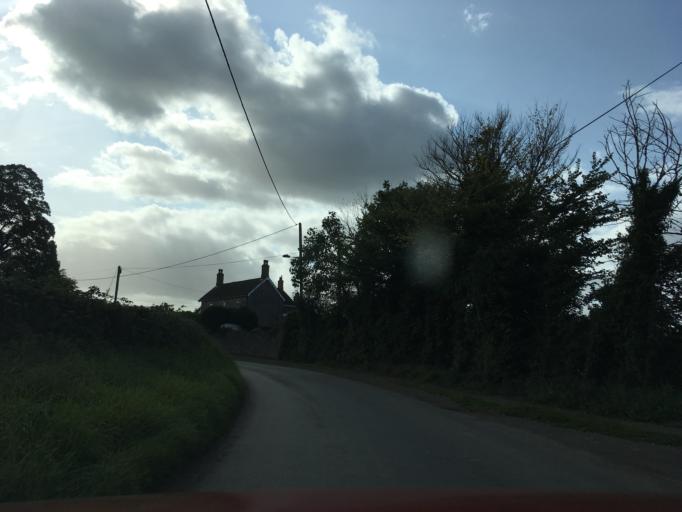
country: GB
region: England
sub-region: South Gloucestershire
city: Wickwar
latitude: 51.5974
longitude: -2.4075
